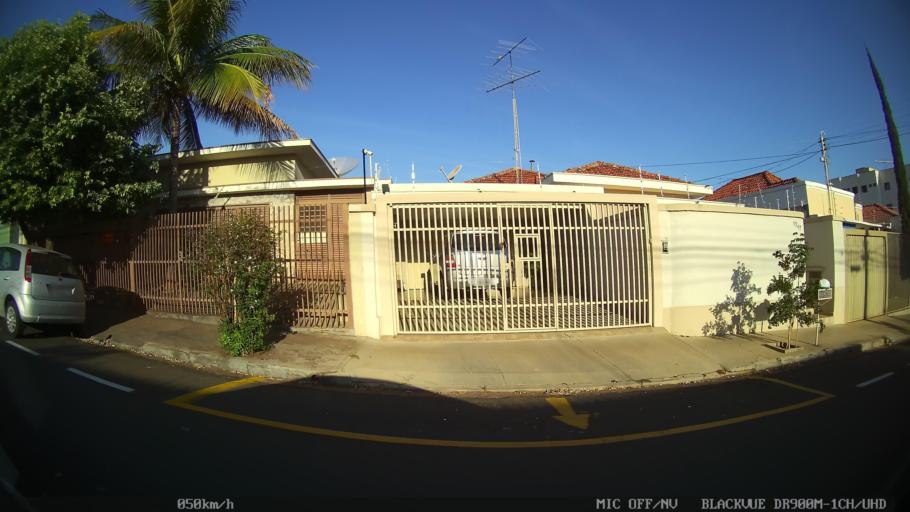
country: BR
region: Sao Paulo
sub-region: Sao Jose Do Rio Preto
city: Sao Jose do Rio Preto
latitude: -20.8048
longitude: -49.3713
